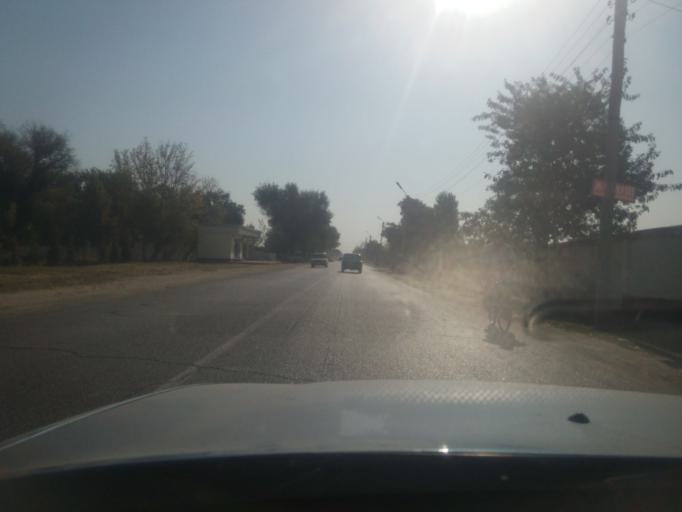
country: UZ
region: Sirdaryo
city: Guliston
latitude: 40.4946
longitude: 68.7940
